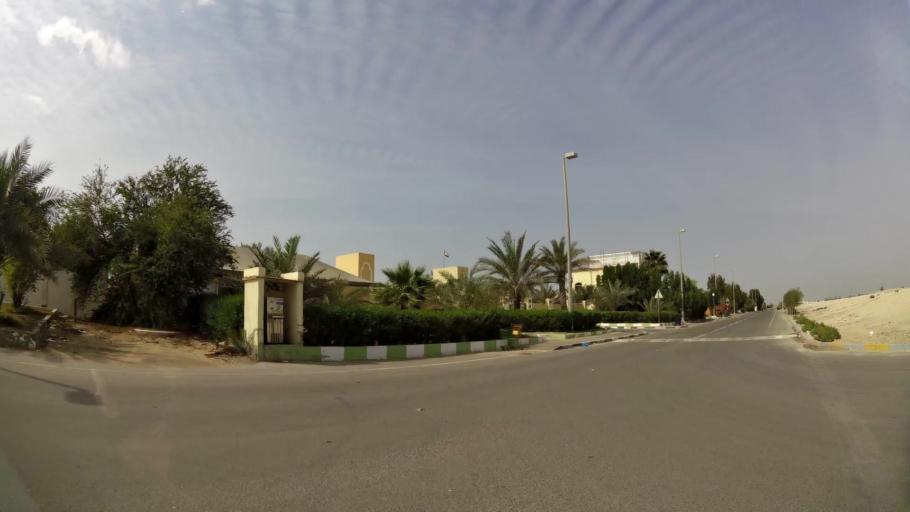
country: AE
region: Abu Dhabi
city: Abu Dhabi
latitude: 24.5560
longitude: 54.6924
